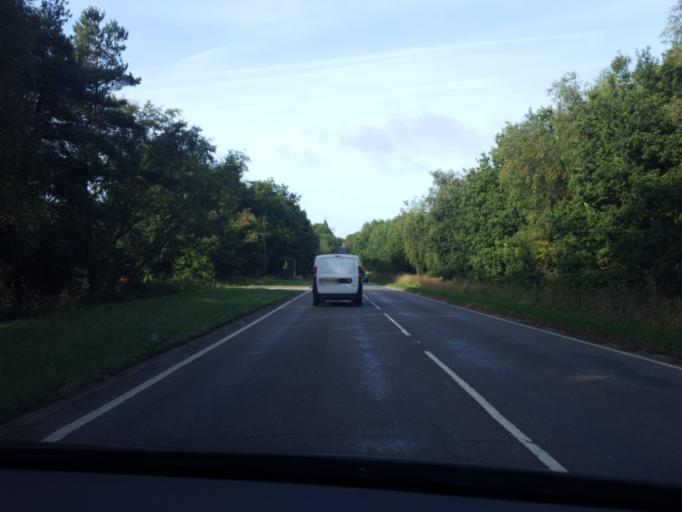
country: GB
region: England
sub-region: Leicestershire
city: Markfield
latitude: 52.7088
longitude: -1.2927
